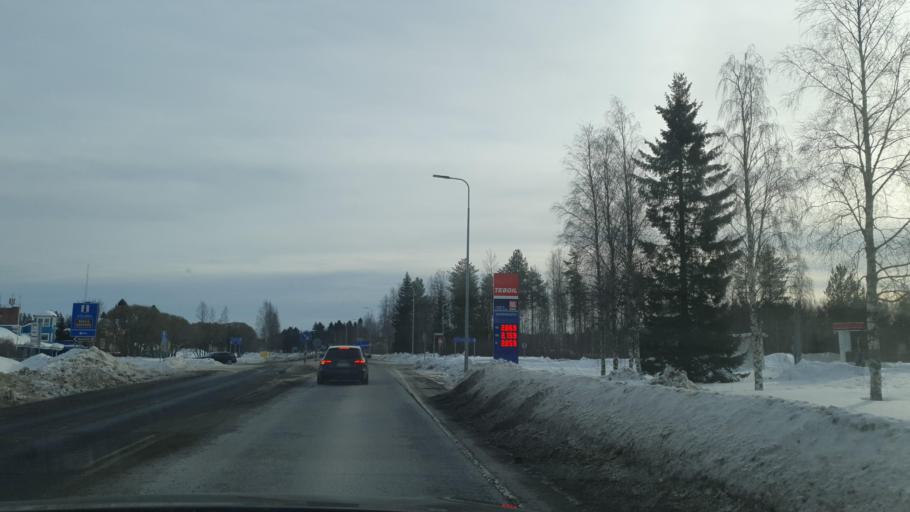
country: FI
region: Northern Ostrobothnia
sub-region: Oulunkaari
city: Utajaervi
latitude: 64.7629
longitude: 26.4108
